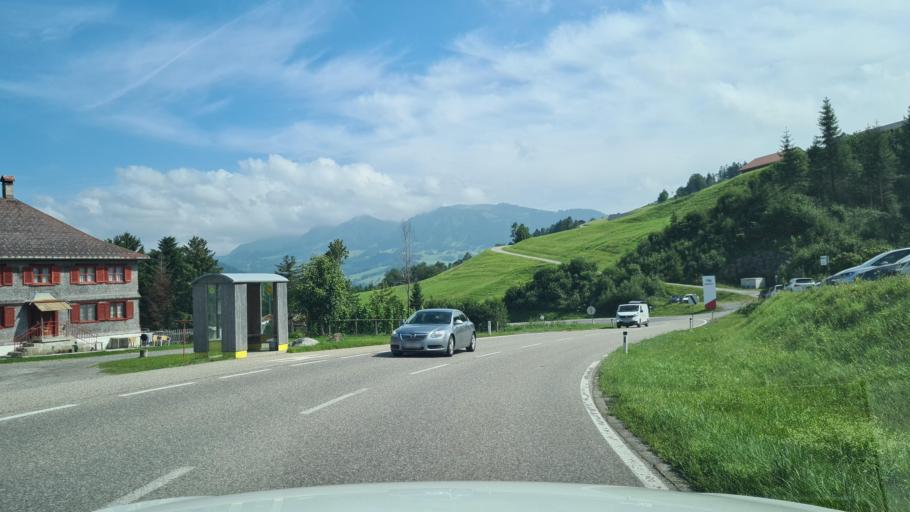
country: AT
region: Vorarlberg
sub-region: Politischer Bezirk Bregenz
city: Doren
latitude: 47.4571
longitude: 9.8672
